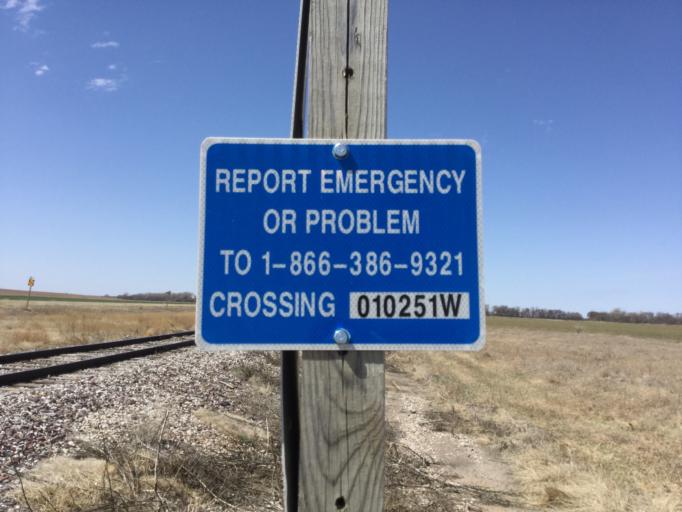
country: US
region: Kansas
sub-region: Barton County
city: Hoisington
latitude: 38.4565
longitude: -99.0147
